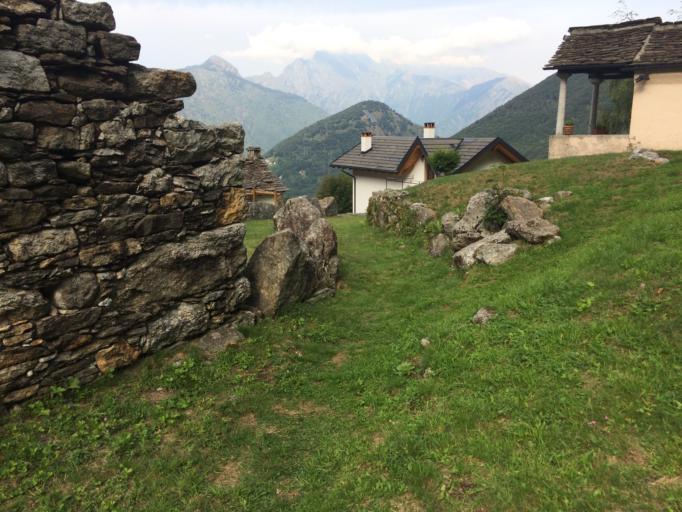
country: IT
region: Piedmont
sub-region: Provincia Verbano-Cusio-Ossola
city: Gurro
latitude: 46.0762
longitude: 8.5346
